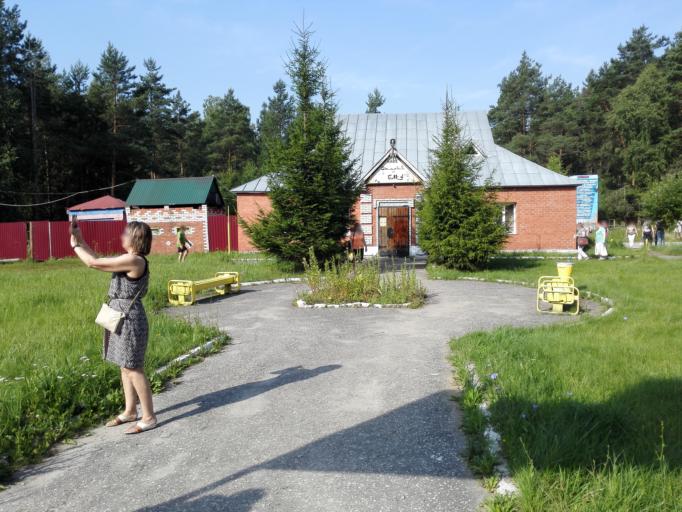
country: RU
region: Vladimir
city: Kurlovo
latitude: 55.4614
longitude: 40.5885
